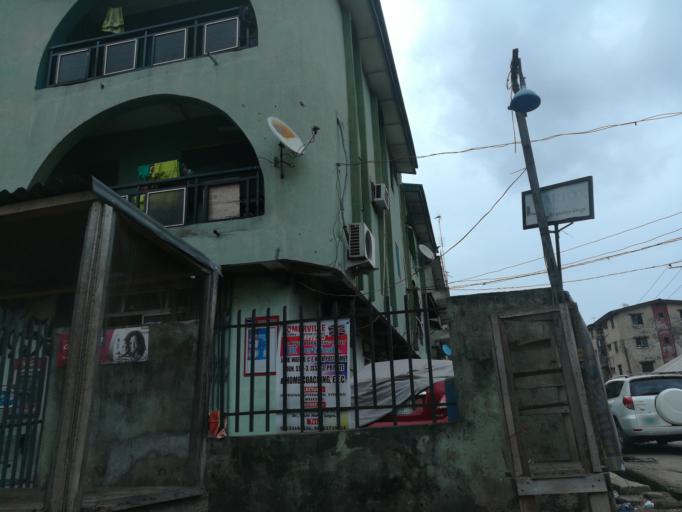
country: NG
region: Lagos
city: Ebute Metta
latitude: 6.4846
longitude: 3.3880
